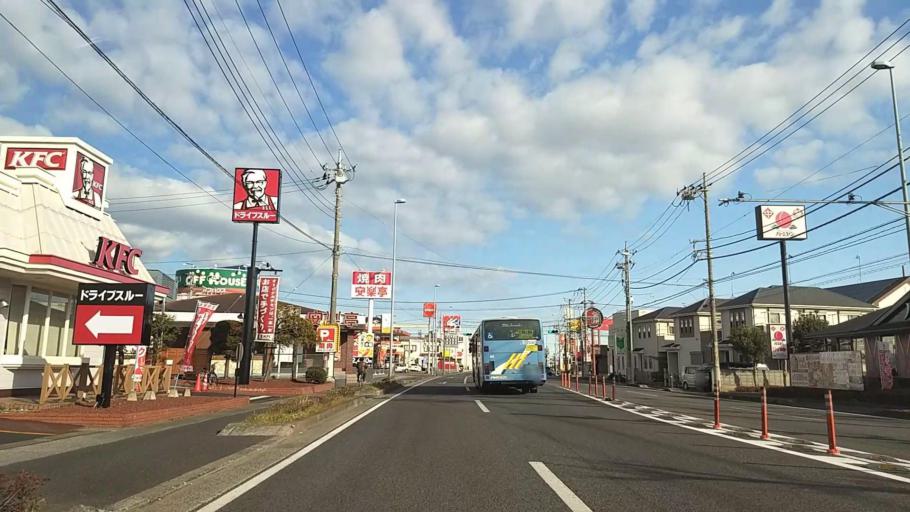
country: JP
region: Kanagawa
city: Hiratsuka
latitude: 35.3587
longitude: 139.3583
